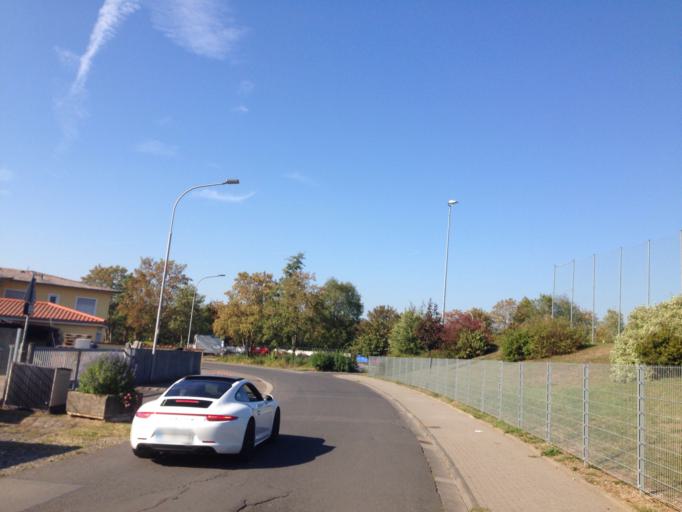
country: DE
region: Hesse
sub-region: Regierungsbezirk Giessen
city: Giessen
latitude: 50.5433
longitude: 8.7096
